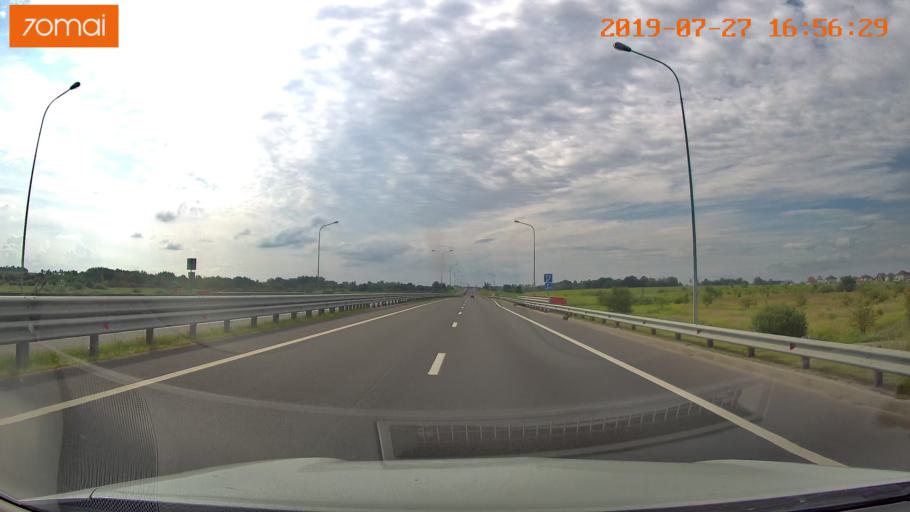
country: RU
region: Kaliningrad
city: Bol'shoe Isakovo
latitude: 54.6949
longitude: 20.7380
